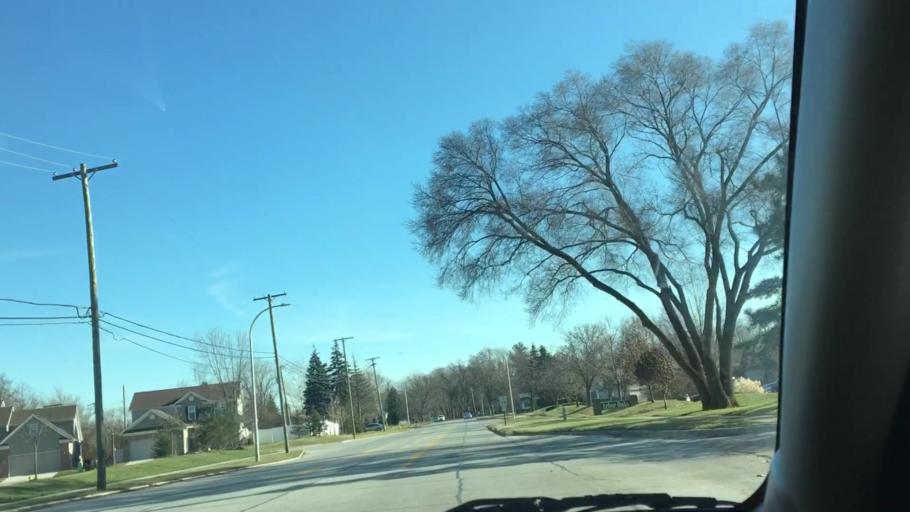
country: US
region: Michigan
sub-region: Wayne County
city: Livonia
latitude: 42.3482
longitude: -83.3676
